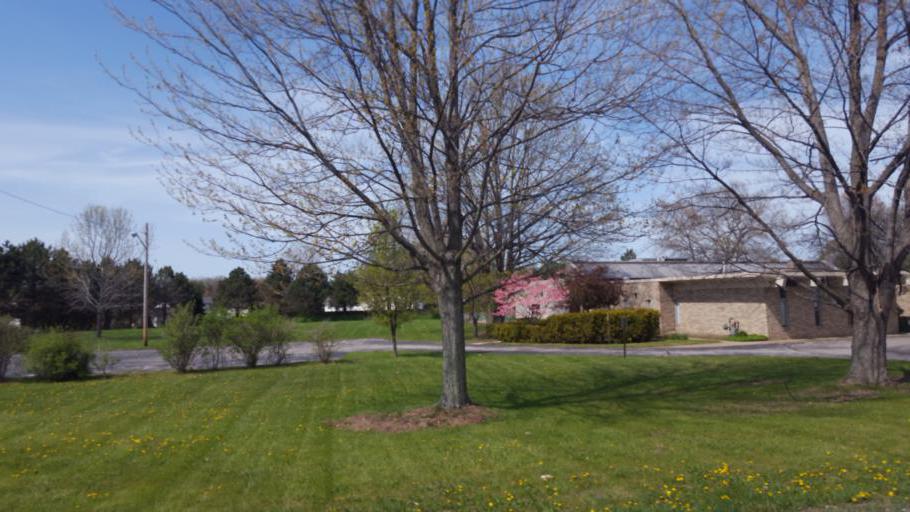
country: US
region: Ohio
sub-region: Lake County
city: Fairport Harbor
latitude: 41.7276
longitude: -81.2975
